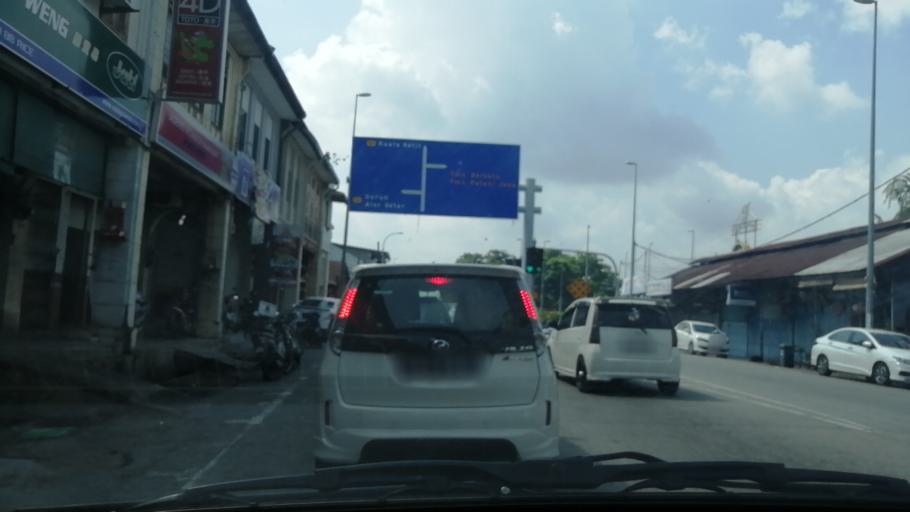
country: MY
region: Kedah
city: Sungai Petani
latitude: 5.6390
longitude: 100.4925
